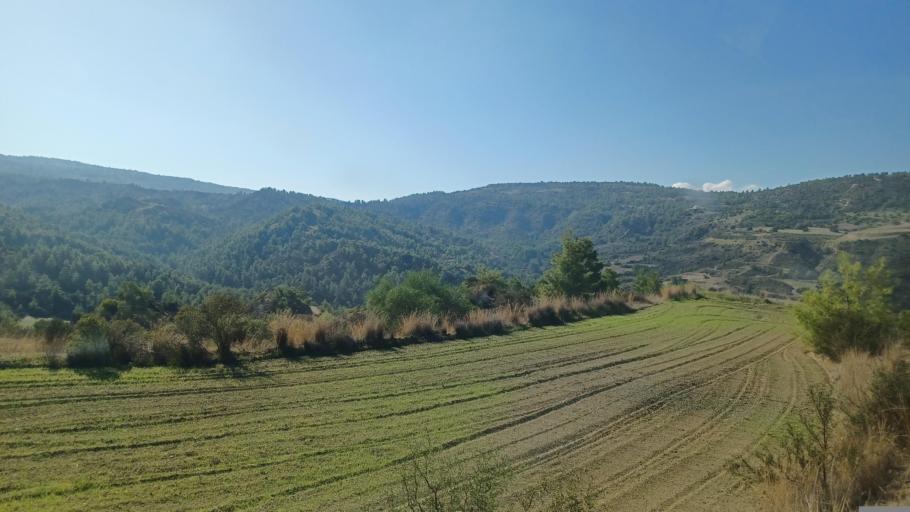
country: CY
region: Pafos
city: Polis
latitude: 35.0331
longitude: 32.4939
